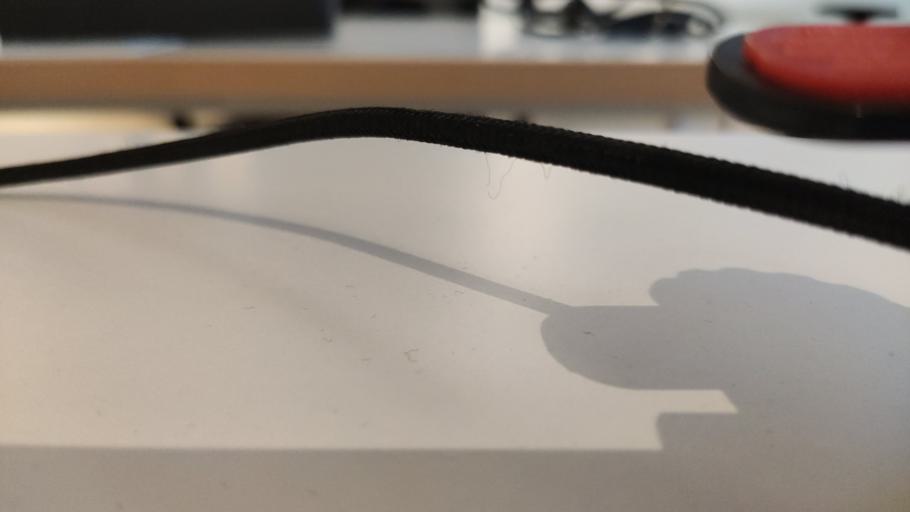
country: RU
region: Moskovskaya
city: Ruza
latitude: 55.7993
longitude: 36.2888
